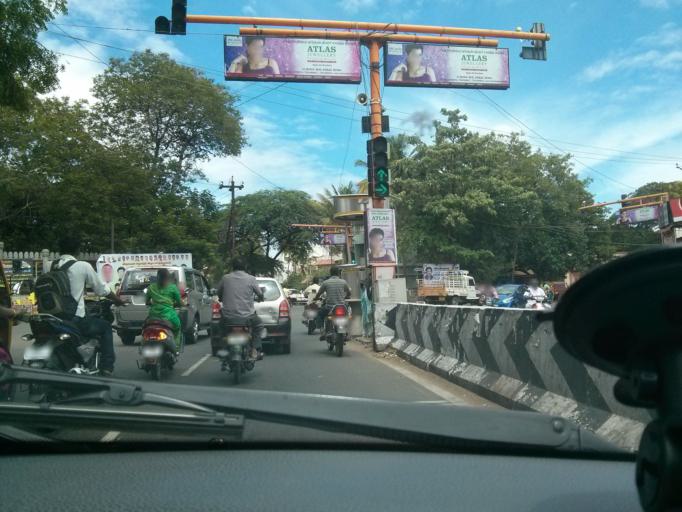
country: IN
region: Tamil Nadu
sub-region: Coimbatore
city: Coimbatore
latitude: 11.0136
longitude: 76.9419
